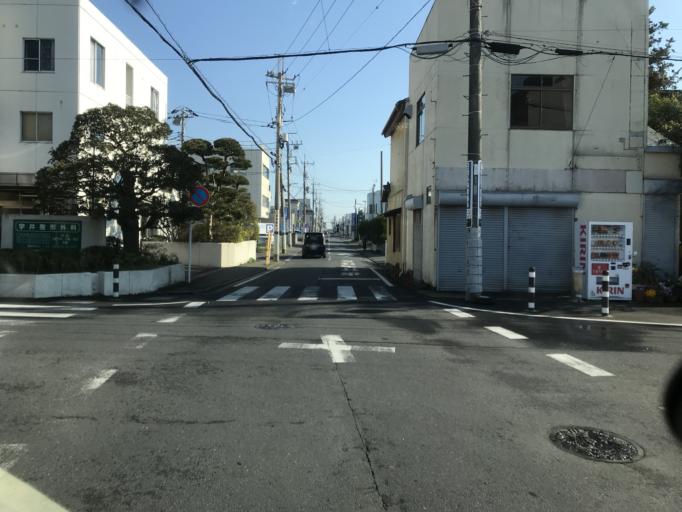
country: JP
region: Chiba
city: Katori-shi
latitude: 35.8950
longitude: 140.4964
